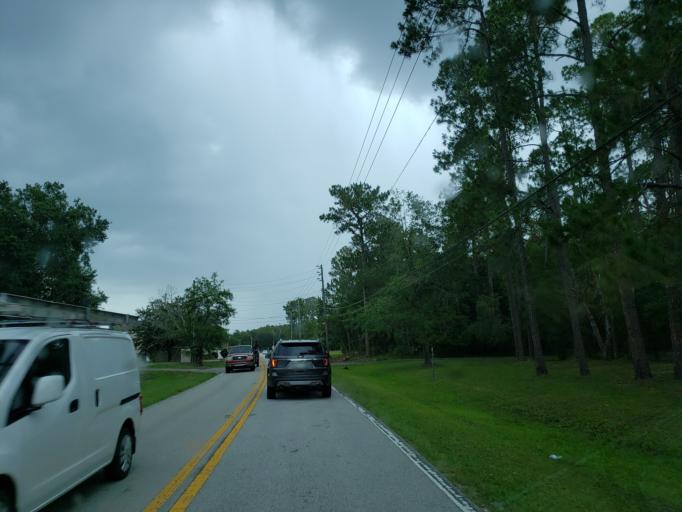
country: US
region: Florida
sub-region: Pasco County
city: Wesley Chapel
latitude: 28.2577
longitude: -82.3544
